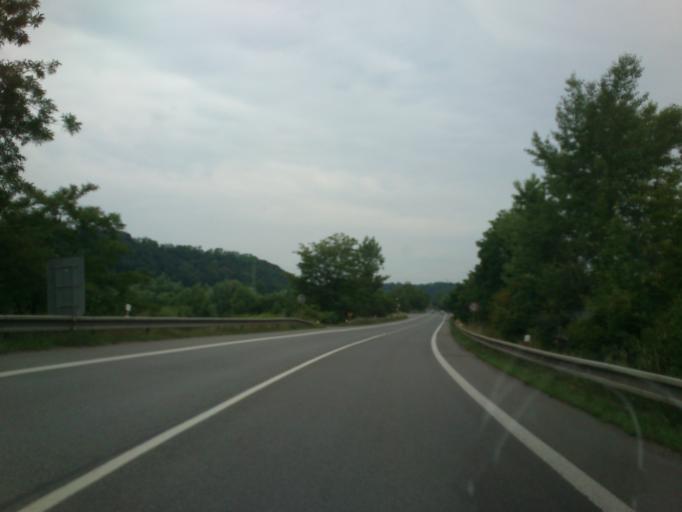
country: CZ
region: Central Bohemia
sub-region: Okres Mlada Boleslav
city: Mlada Boleslav
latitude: 50.4379
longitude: 14.8916
